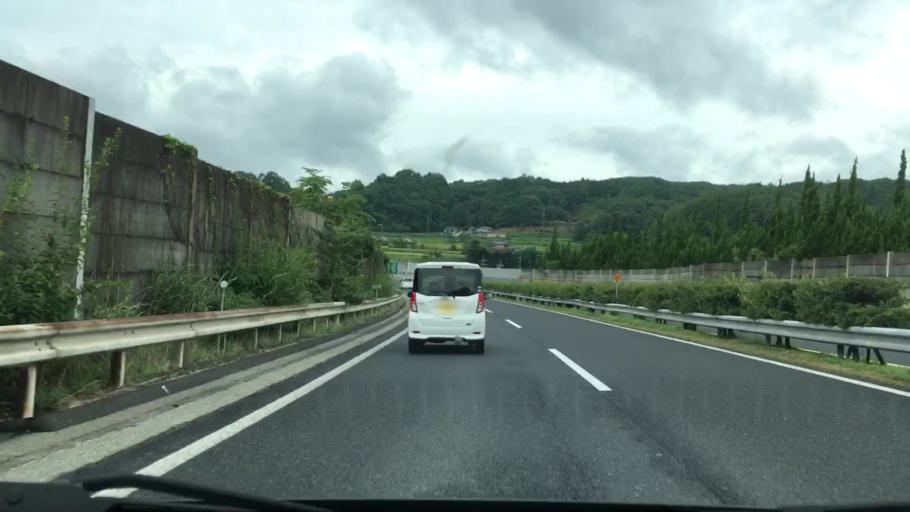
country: JP
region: Okayama
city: Tsuyama
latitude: 35.0182
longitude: 134.2265
